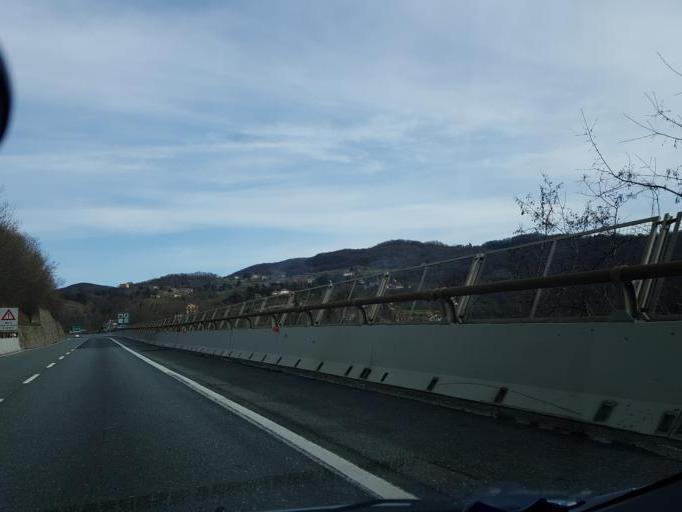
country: IT
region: Liguria
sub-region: Provincia di Genova
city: Serra Ricco
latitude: 44.5244
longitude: 8.9371
